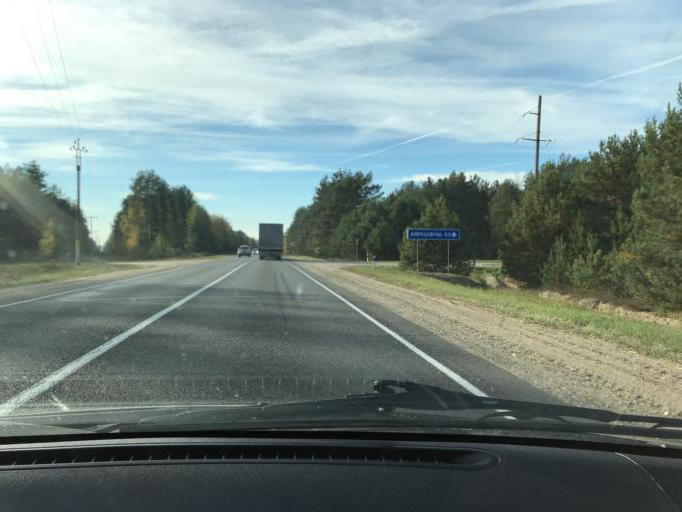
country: BY
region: Brest
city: Horad Pinsk
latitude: 52.1509
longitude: 25.8508
